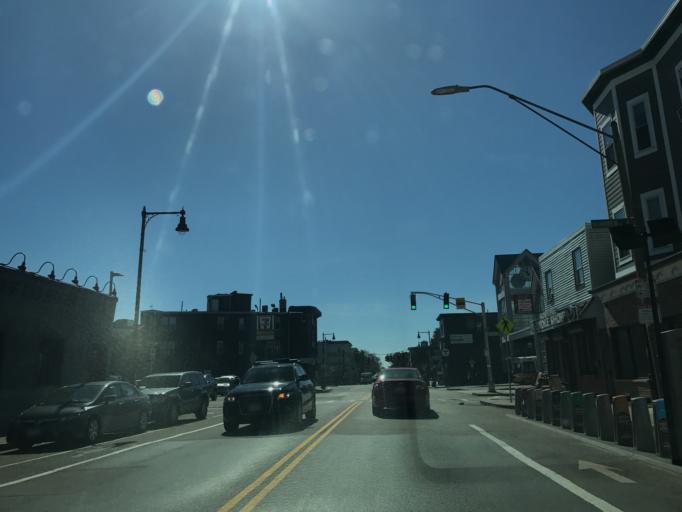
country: US
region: Massachusetts
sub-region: Suffolk County
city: South Boston
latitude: 42.3306
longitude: -71.0570
